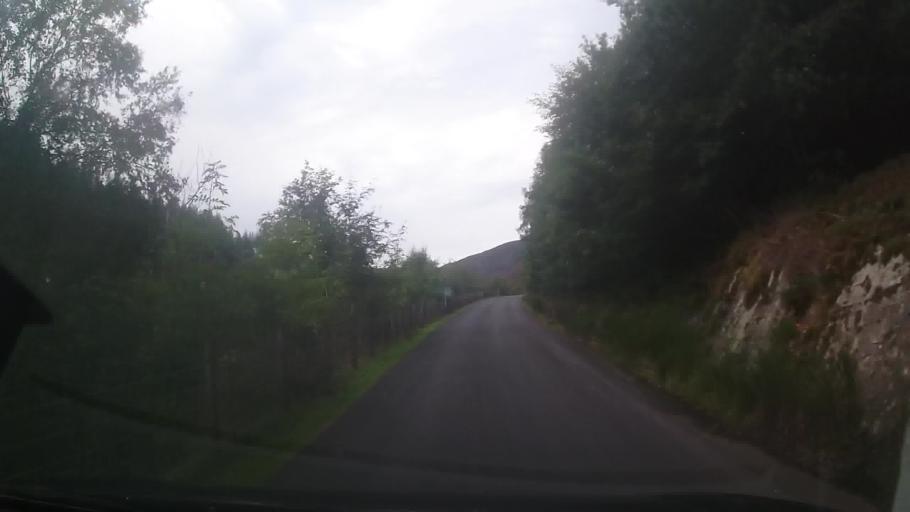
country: GB
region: Wales
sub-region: Sir Powys
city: Rhayader
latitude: 52.2838
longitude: -3.5944
